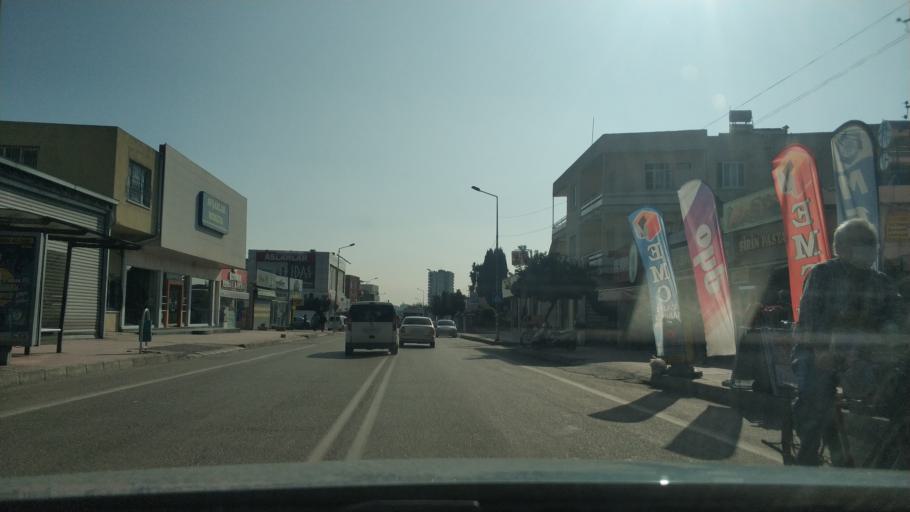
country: TR
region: Adana
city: Seyhan
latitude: 37.0163
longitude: 35.3004
